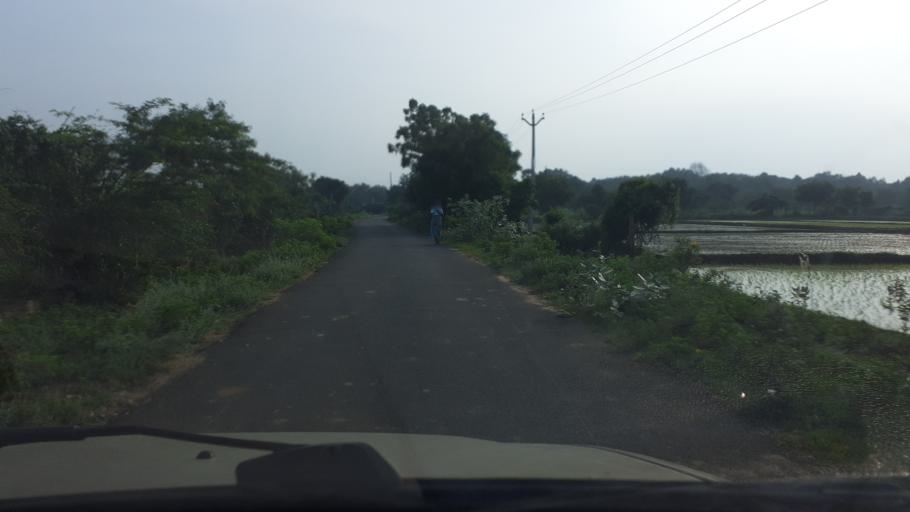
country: IN
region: Tamil Nadu
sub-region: Tirunelveli Kattabo
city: Kalakkadu
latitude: 8.4698
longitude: 77.5851
